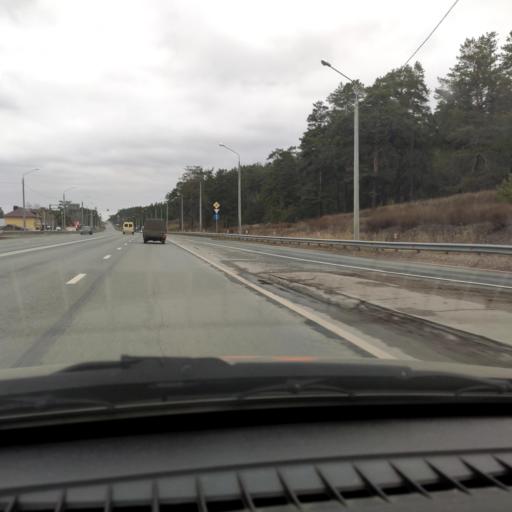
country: RU
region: Samara
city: Volzhskiy
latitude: 53.4359
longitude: 50.1129
